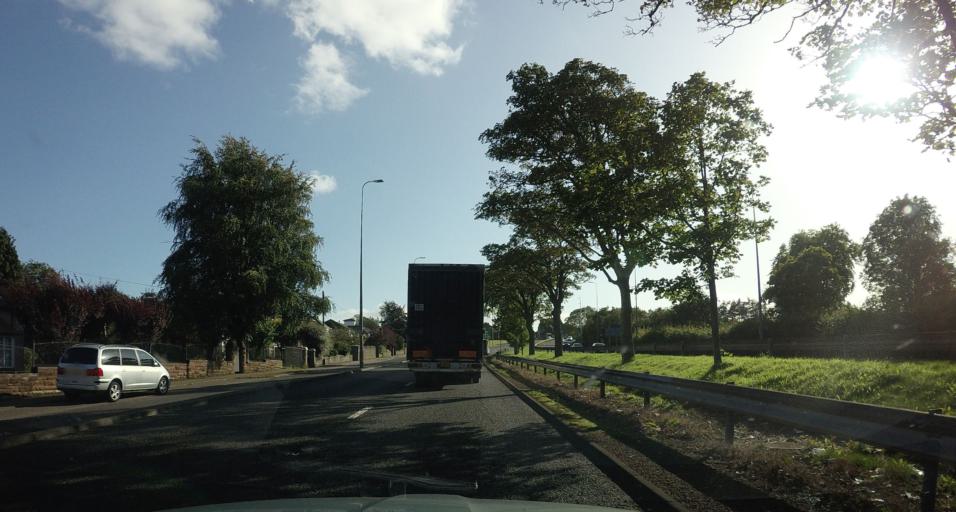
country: GB
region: Scotland
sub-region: Dundee City
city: Dundee
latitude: 56.4822
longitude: -2.9518
